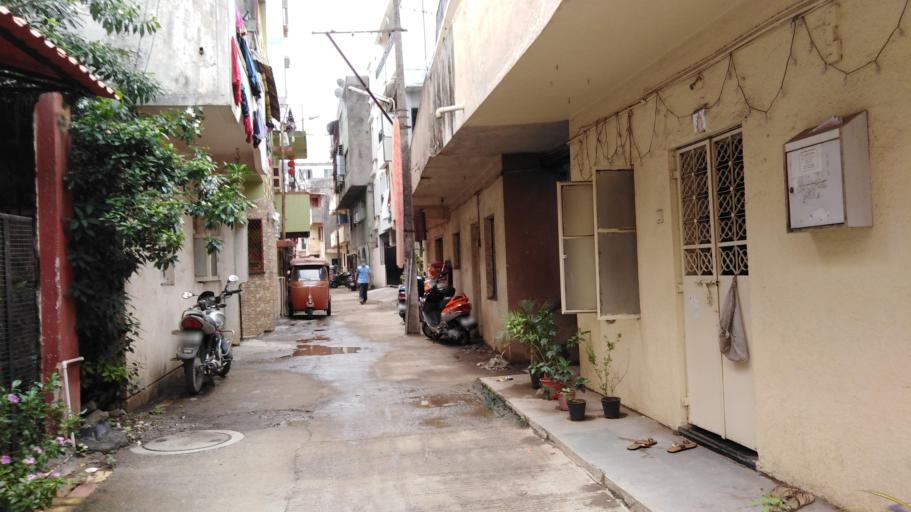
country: IN
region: Maharashtra
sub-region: Pune Division
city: Pune
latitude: 18.4797
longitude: 73.8284
